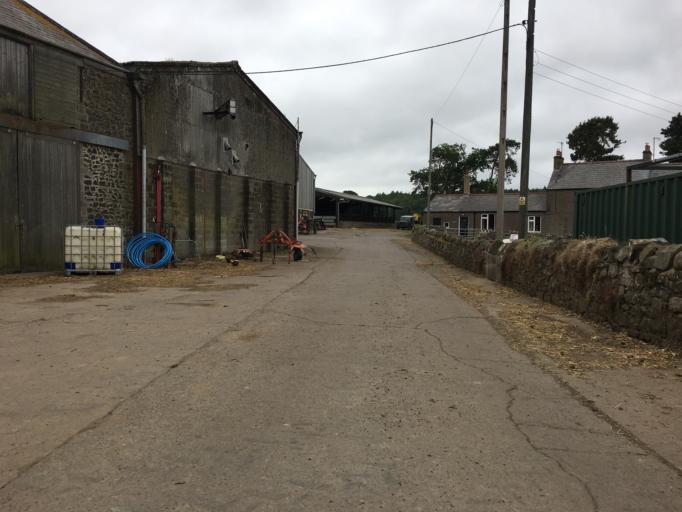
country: GB
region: England
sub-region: Northumberland
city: Belford
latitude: 55.6084
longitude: -1.8673
